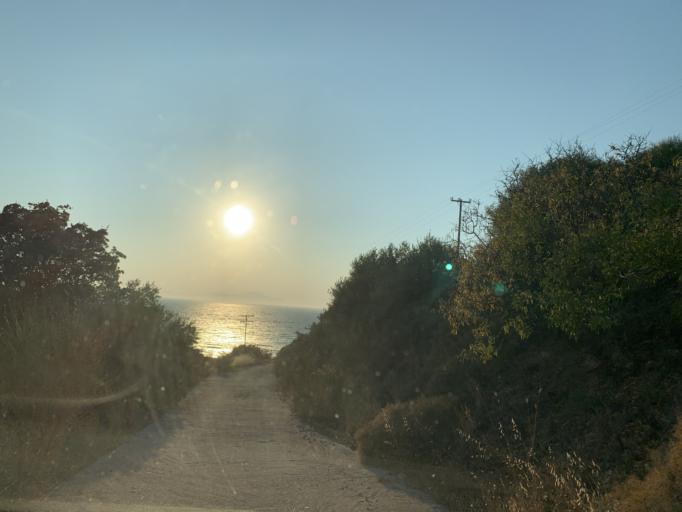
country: GR
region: North Aegean
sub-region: Chios
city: Psara
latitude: 38.5222
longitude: 25.8491
